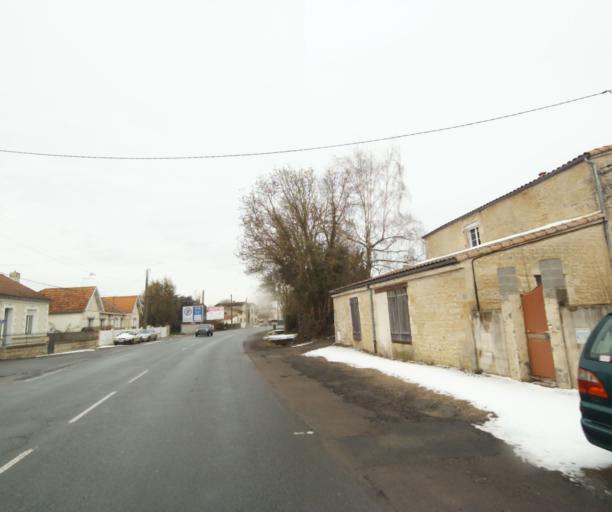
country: FR
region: Poitou-Charentes
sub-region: Departement des Deux-Sevres
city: Niort
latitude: 46.3040
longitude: -0.4657
